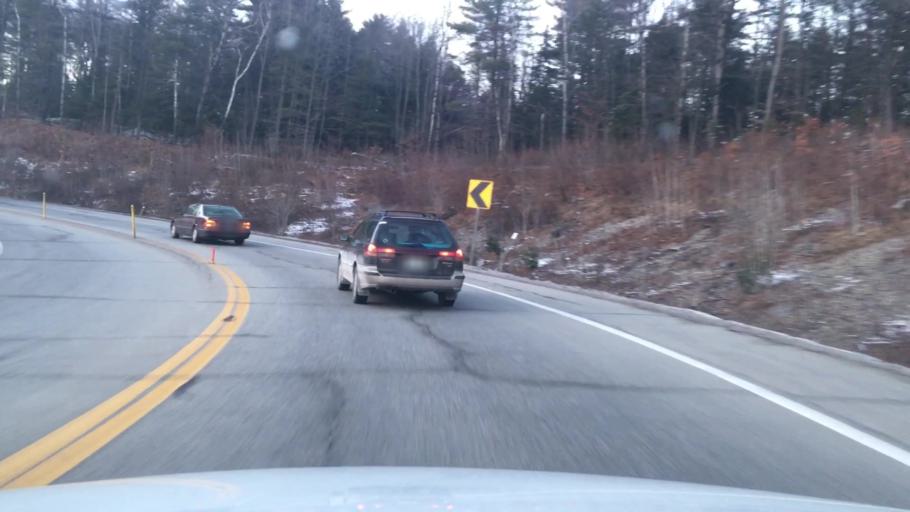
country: US
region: Maine
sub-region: Androscoggin County
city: Minot
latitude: 44.0388
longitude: -70.2690
